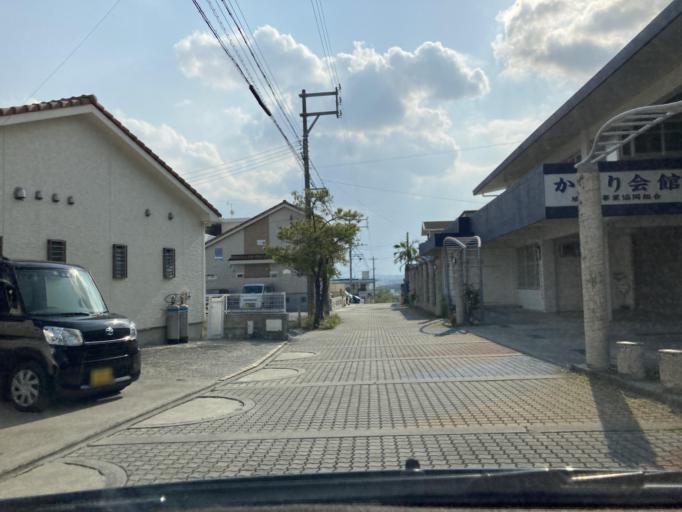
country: JP
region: Okinawa
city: Tomigusuku
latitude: 26.1895
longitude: 127.7279
